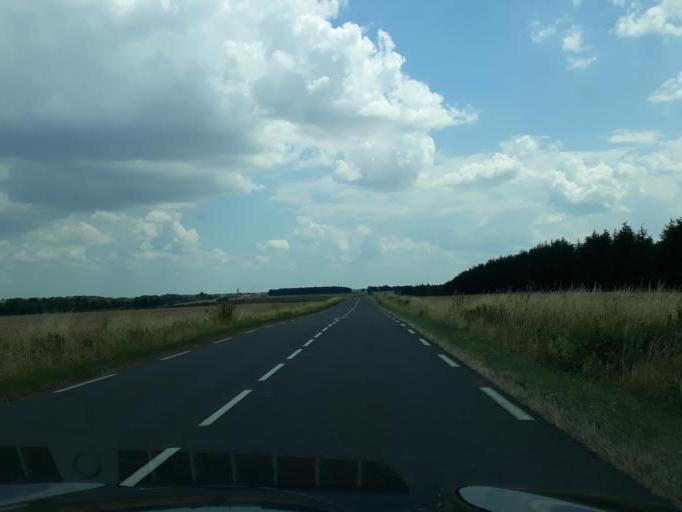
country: FR
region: Centre
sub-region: Departement du Cher
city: Avord
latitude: 47.0374
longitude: 2.6017
